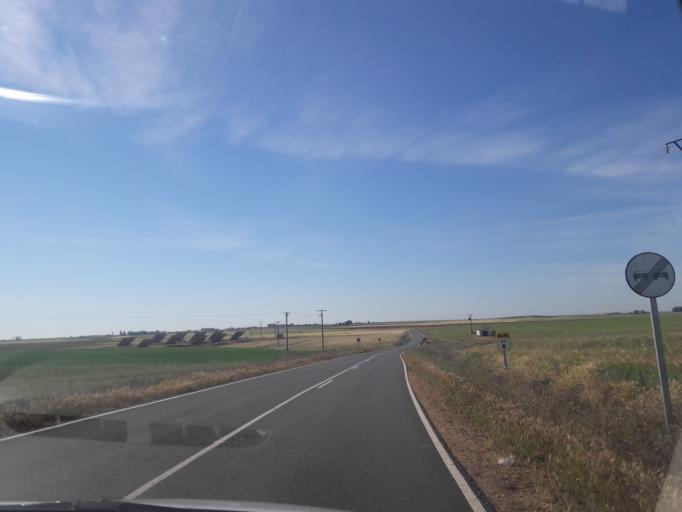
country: ES
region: Castille and Leon
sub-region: Provincia de Salamanca
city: Espino de la Orbada
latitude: 41.1014
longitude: -5.4188
